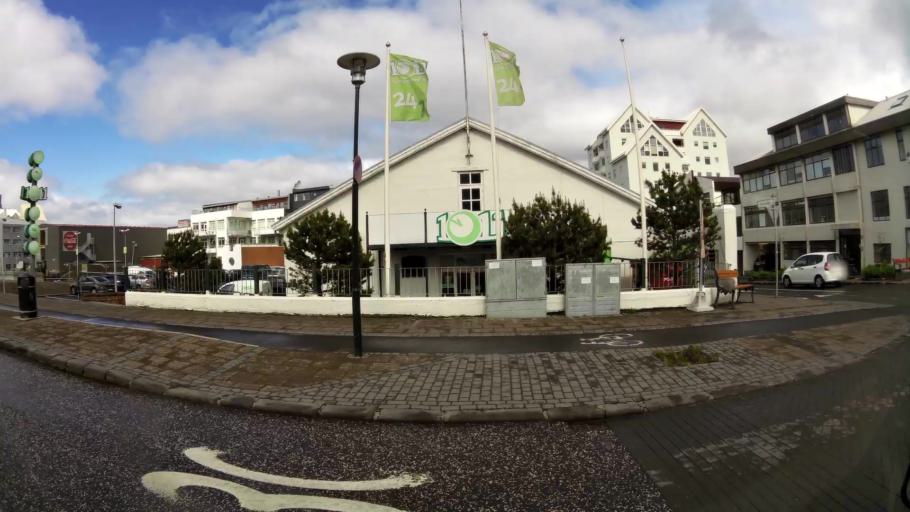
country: IS
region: Capital Region
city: Reykjavik
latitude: 64.1443
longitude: -21.9187
